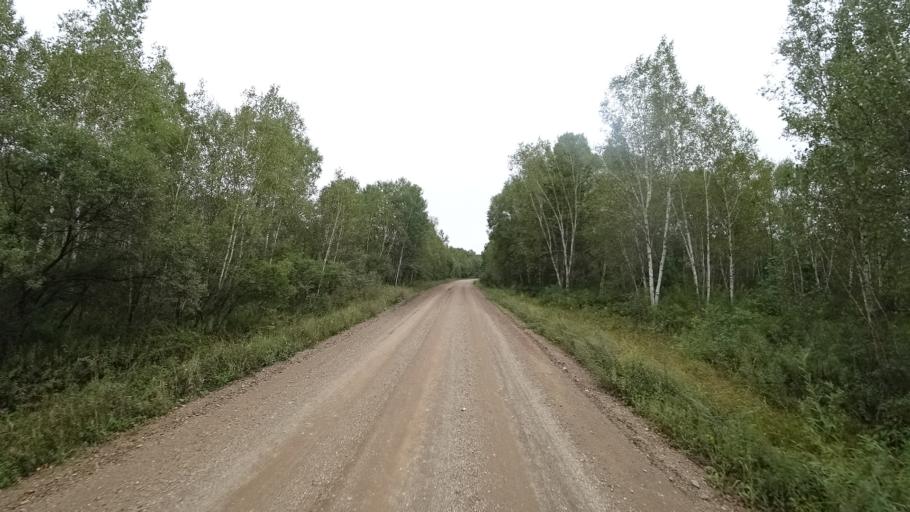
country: RU
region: Primorskiy
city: Ivanovka
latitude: 44.0280
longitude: 132.5142
